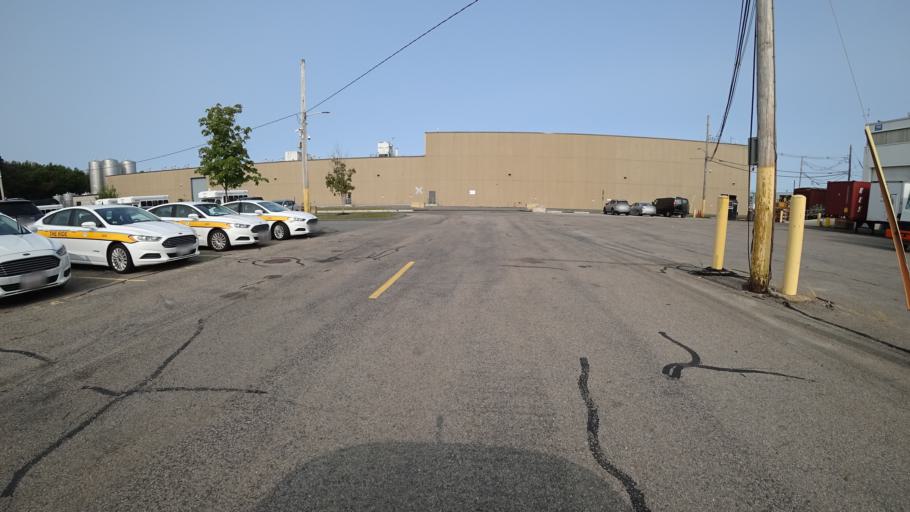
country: US
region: Massachusetts
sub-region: Norfolk County
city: Dedham
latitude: 42.2291
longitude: -71.1350
